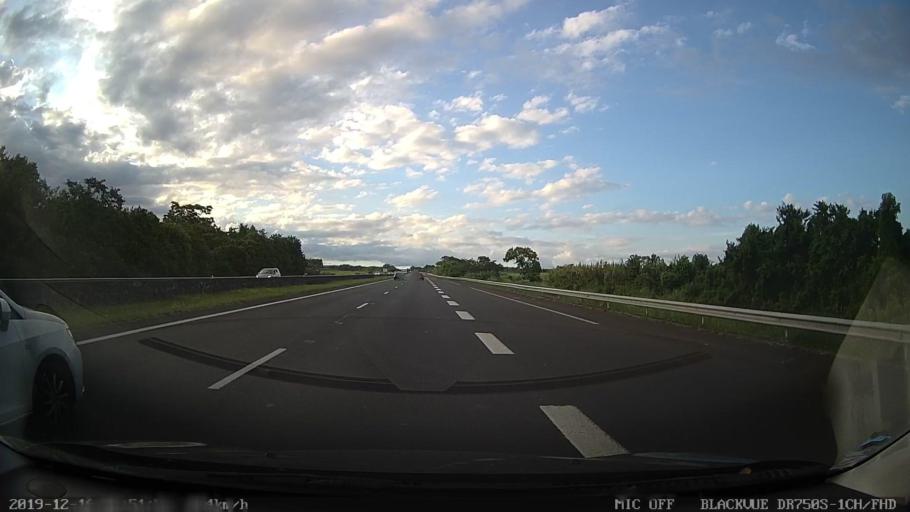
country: RE
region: Reunion
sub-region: Reunion
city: Bras-Panon
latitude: -20.9989
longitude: 55.6731
